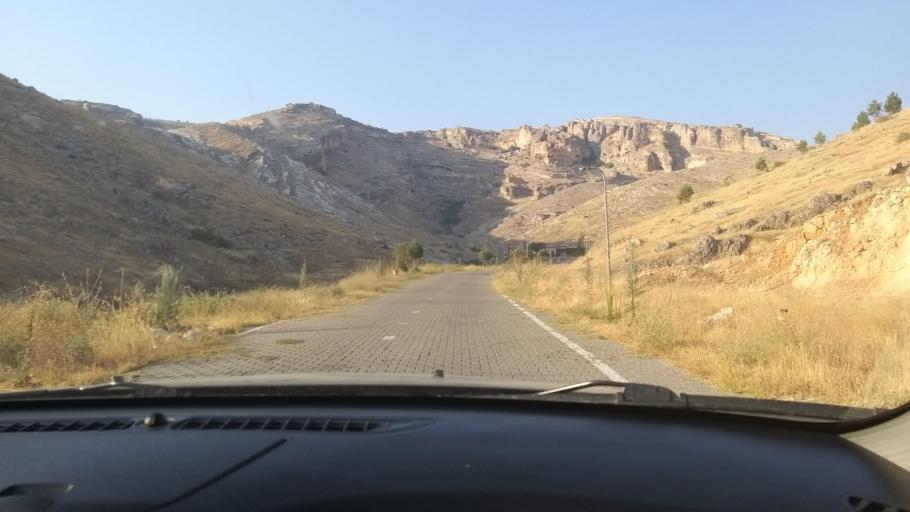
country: TR
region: Diyarbakir
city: Silvan
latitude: 38.1293
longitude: 41.0879
